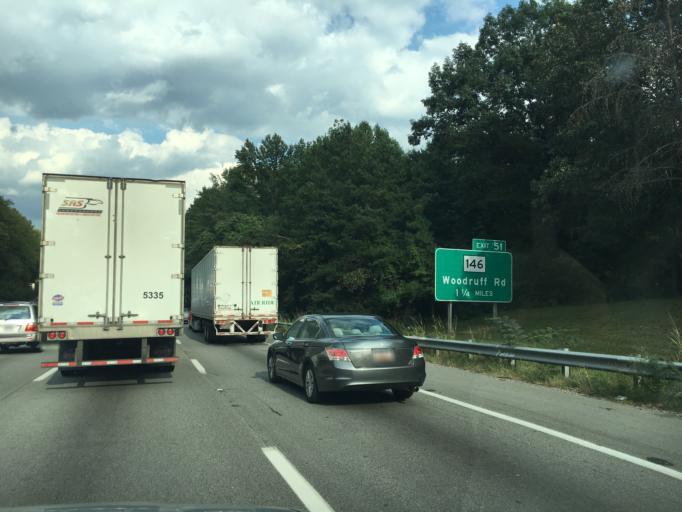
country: US
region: South Carolina
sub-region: Greenville County
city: Mauldin
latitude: 34.8165
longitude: -82.3259
